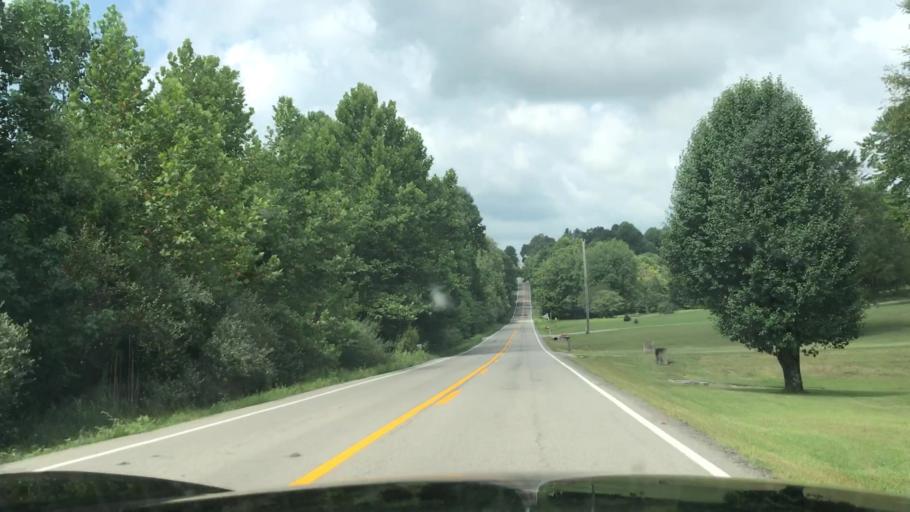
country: US
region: Kentucky
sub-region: Muhlenberg County
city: Central City
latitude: 37.2039
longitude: -86.9546
